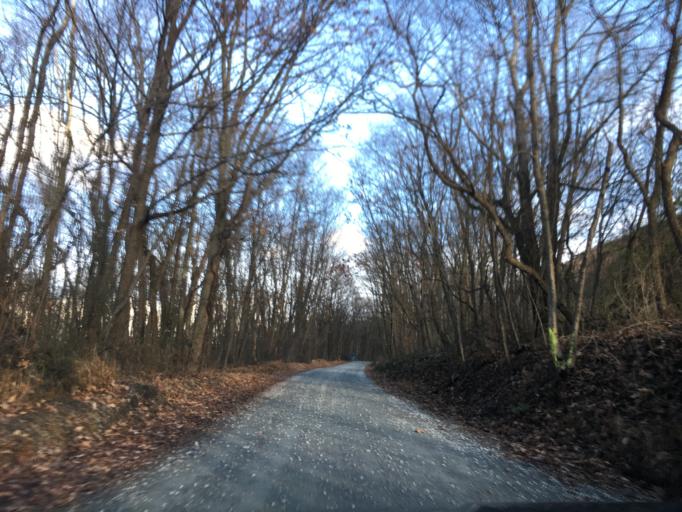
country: US
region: Pennsylvania
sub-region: Carbon County
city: Lehighton
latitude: 40.7688
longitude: -75.7097
